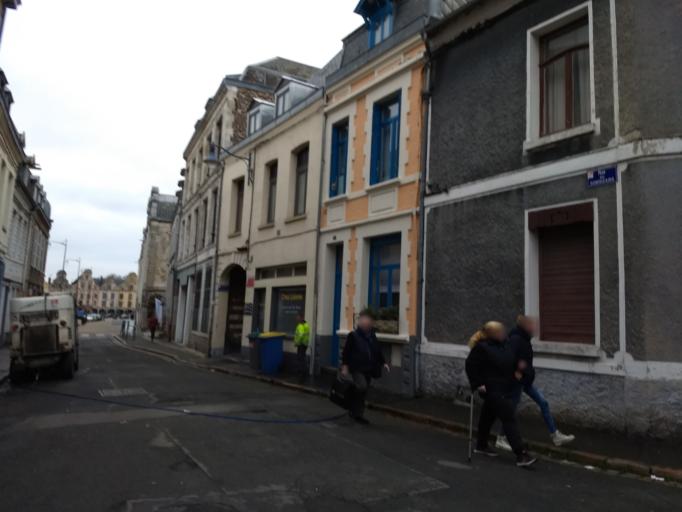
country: FR
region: Nord-Pas-de-Calais
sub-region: Departement du Pas-de-Calais
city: Arras
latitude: 50.2908
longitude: 2.7804
